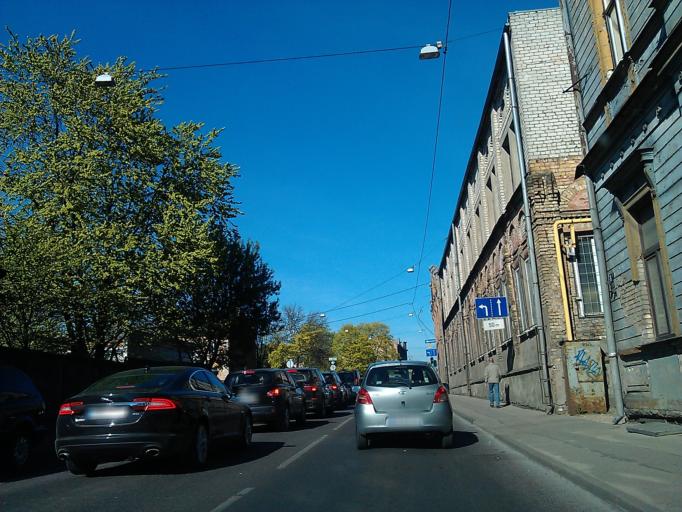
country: LV
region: Riga
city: Riga
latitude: 56.9485
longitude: 24.1448
